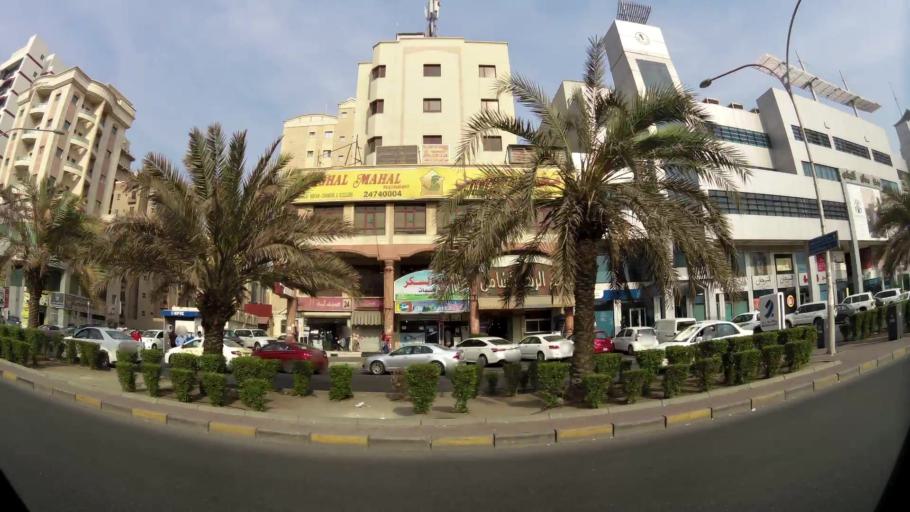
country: KW
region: Al Farwaniyah
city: Al Farwaniyah
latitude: 29.2801
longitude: 47.9610
